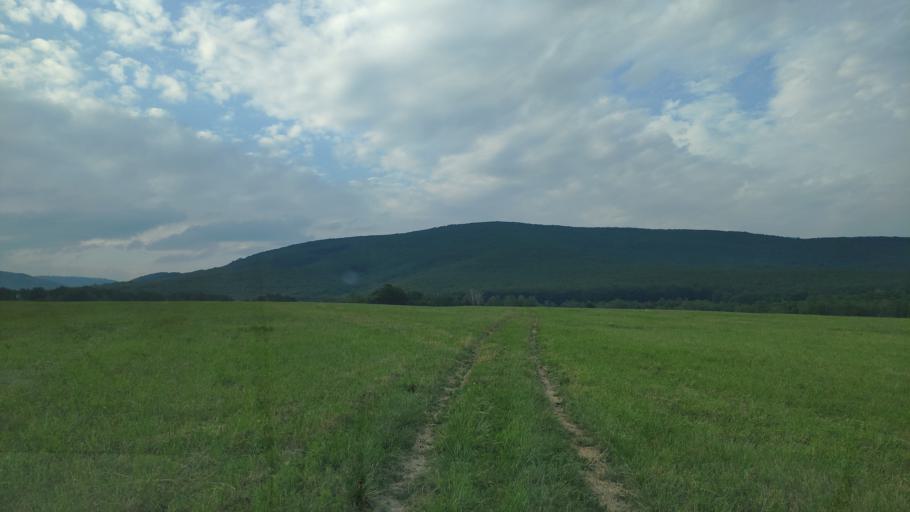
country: SK
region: Kosicky
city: Moldava nad Bodvou
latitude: 48.7122
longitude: 20.9936
